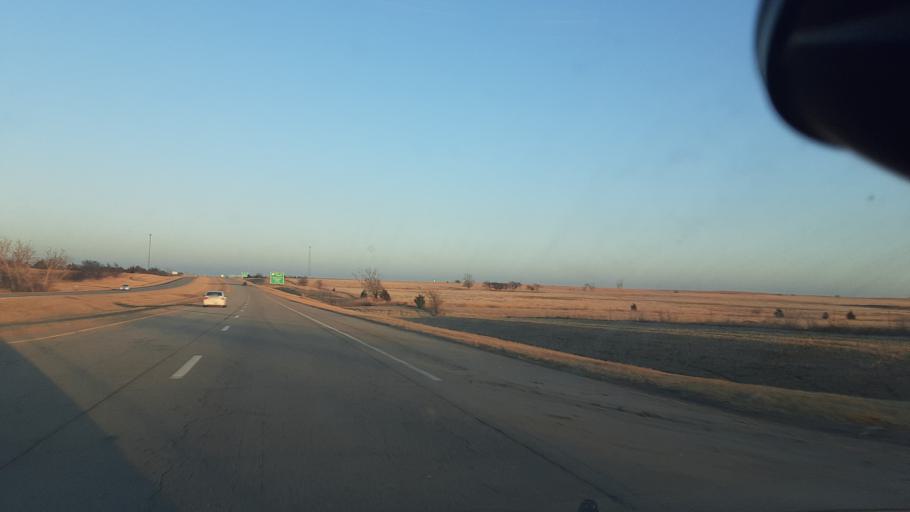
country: US
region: Oklahoma
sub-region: Noble County
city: Perry
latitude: 36.3982
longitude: -97.3544
